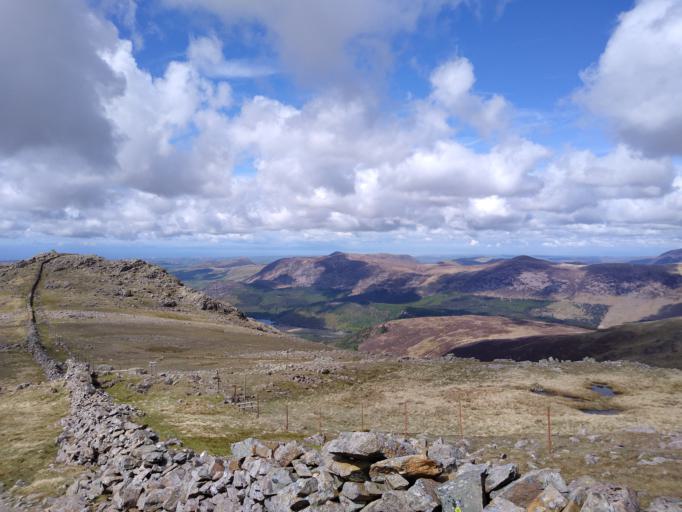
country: GB
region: England
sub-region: Cumbria
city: Seascale
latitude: 54.4852
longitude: -3.3254
